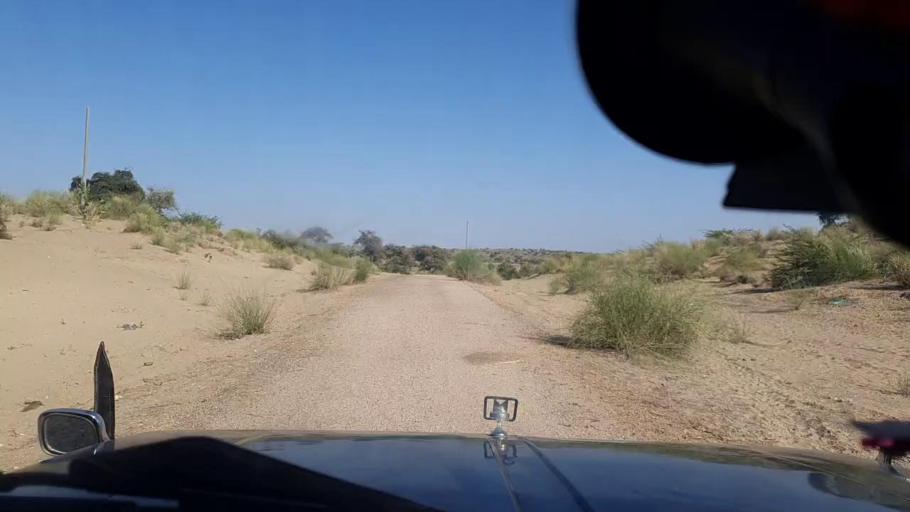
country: PK
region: Sindh
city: Diplo
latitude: 24.4703
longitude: 69.8043
